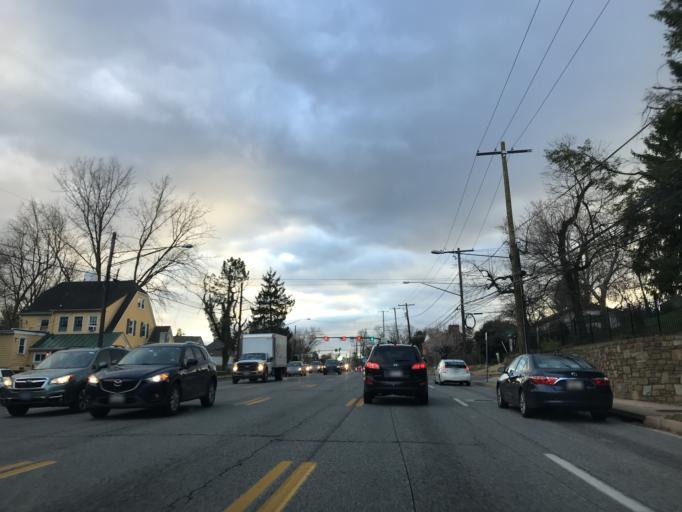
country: US
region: Maryland
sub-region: Montgomery County
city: Four Corners
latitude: 39.0067
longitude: -77.0216
